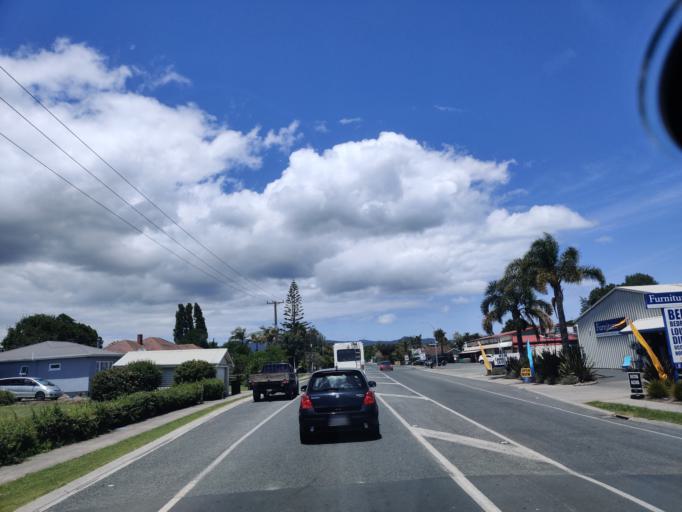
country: NZ
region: Northland
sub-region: Far North District
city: Kaitaia
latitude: -35.1002
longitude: 173.2597
